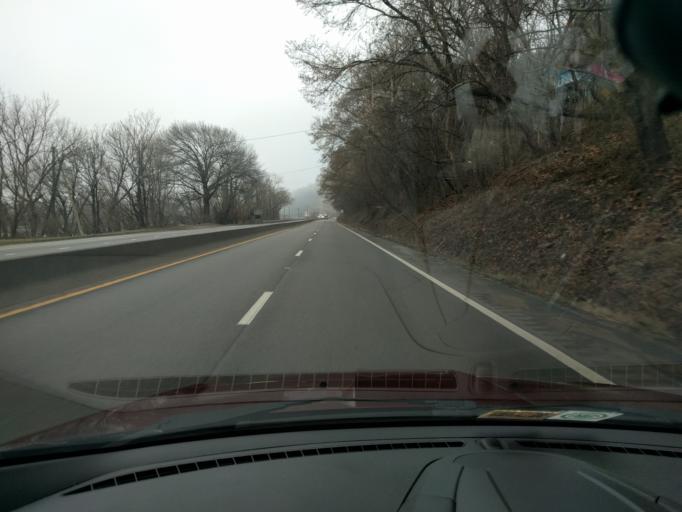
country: US
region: West Virginia
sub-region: Kanawha County
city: Rand
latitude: 38.3025
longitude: -81.5559
